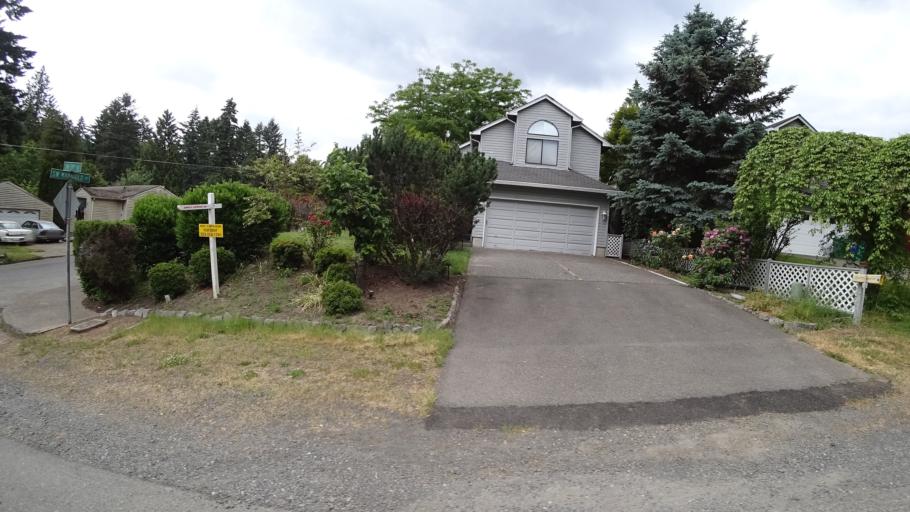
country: US
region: Oregon
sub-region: Clackamas County
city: Lake Oswego
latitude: 45.4604
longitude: -122.6921
